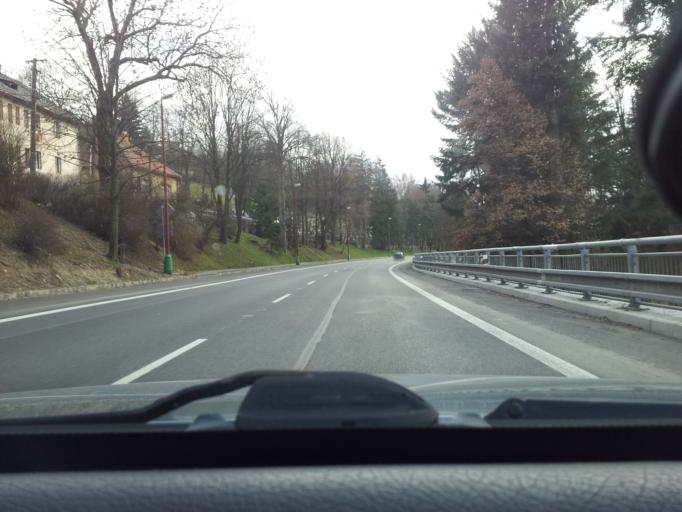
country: SK
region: Banskobystricky
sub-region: Okres Ziar nad Hronom
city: Kremnica
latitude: 48.6971
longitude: 18.9152
